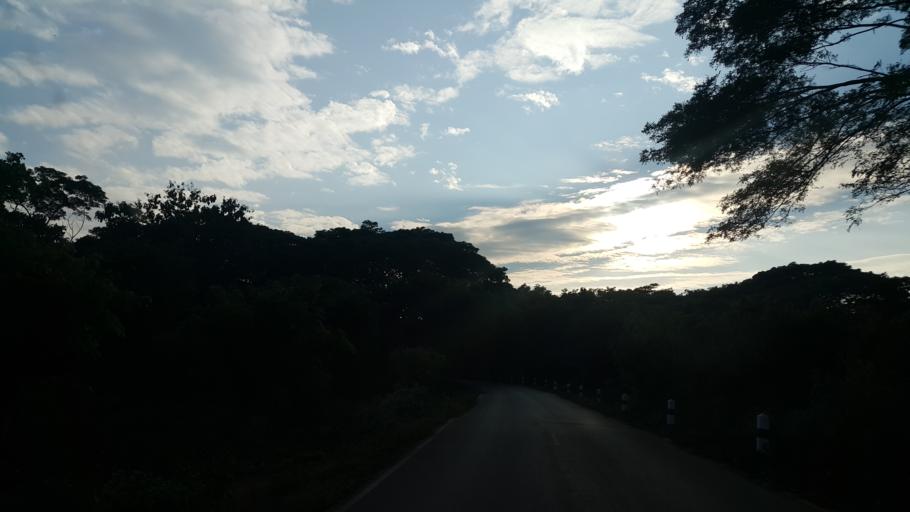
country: TH
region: Lampang
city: Sop Prap
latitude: 17.9229
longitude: 99.3297
